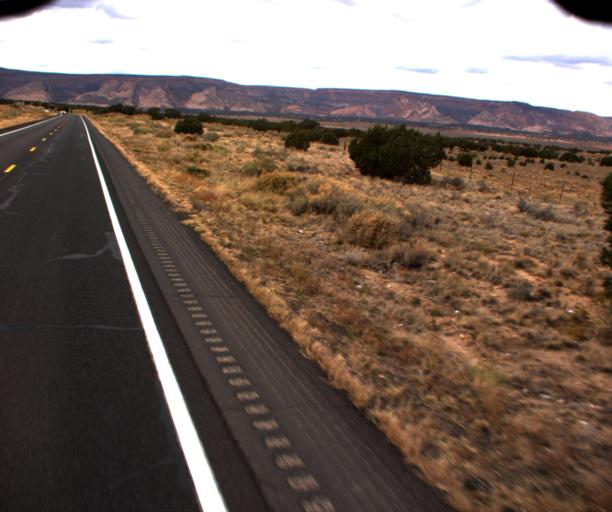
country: US
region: Arizona
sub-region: Navajo County
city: Kayenta
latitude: 36.6986
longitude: -110.3318
